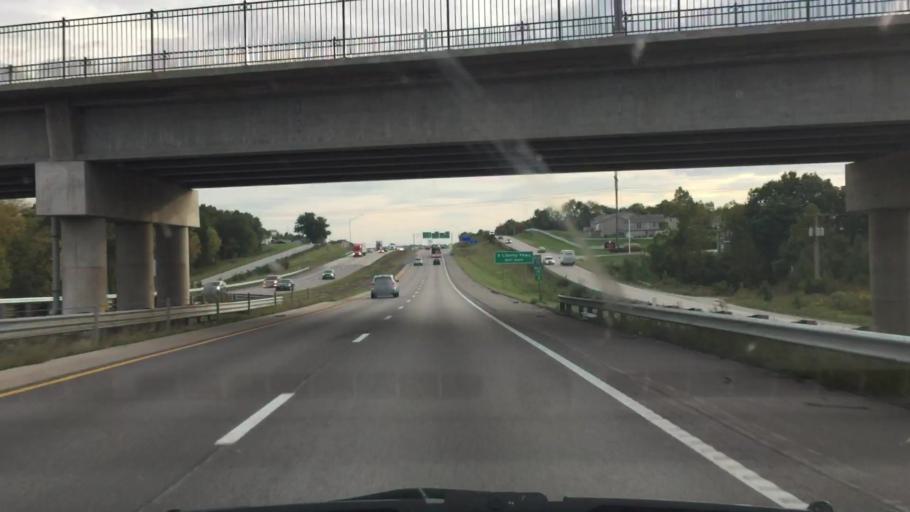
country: US
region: Missouri
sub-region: Clay County
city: Pleasant Valley
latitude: 39.2285
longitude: -94.4672
